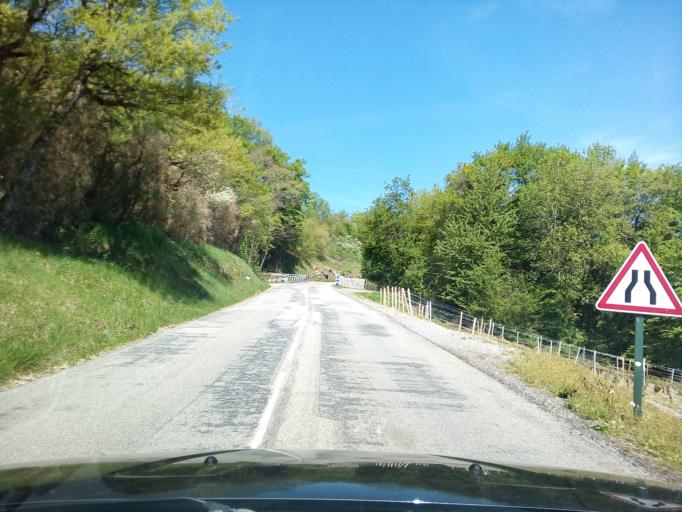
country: FR
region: Rhone-Alpes
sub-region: Departement de l'Isere
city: Chapareillan
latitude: 45.4750
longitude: 5.9761
